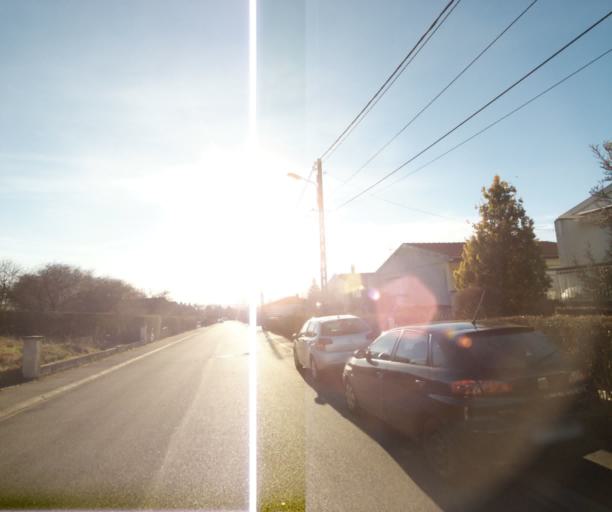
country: FR
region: Lorraine
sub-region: Departement de Meurthe-et-Moselle
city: Seichamps
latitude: 48.7138
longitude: 6.2651
